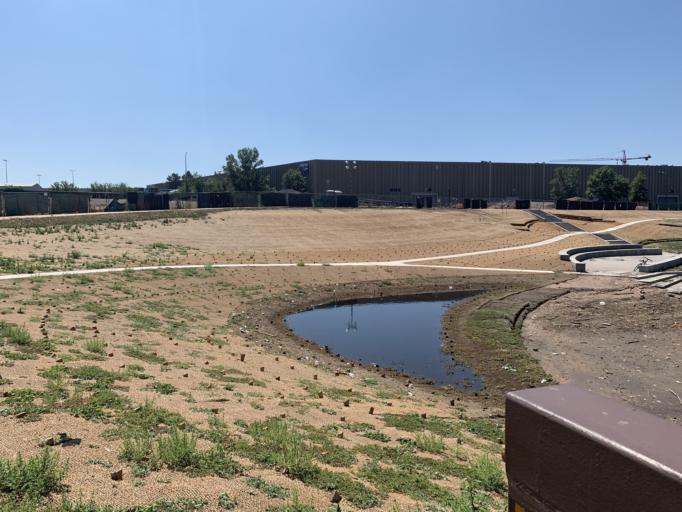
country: US
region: Colorado
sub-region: Denver County
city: Denver
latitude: 39.7772
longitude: -104.9774
